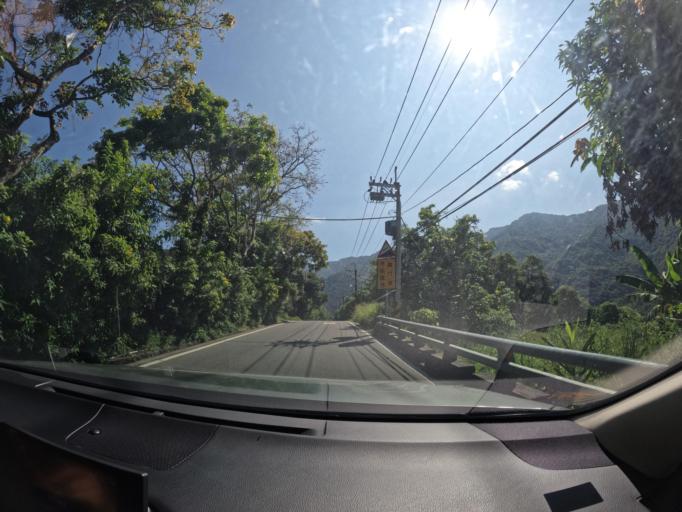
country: TW
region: Taiwan
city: Yujing
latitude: 23.1356
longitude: 120.7254
